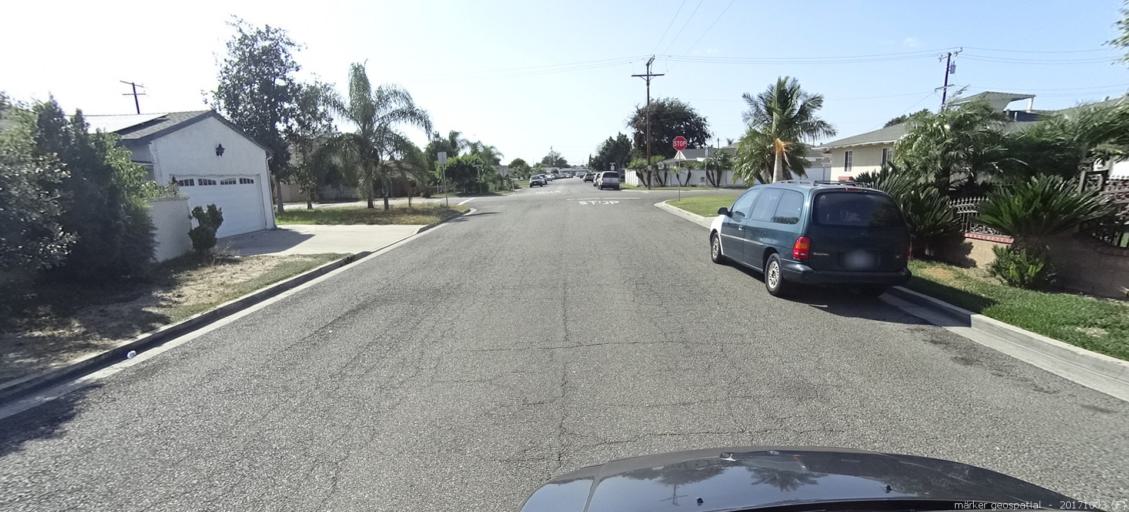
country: US
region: California
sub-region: Orange County
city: Garden Grove
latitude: 33.7698
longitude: -117.9458
